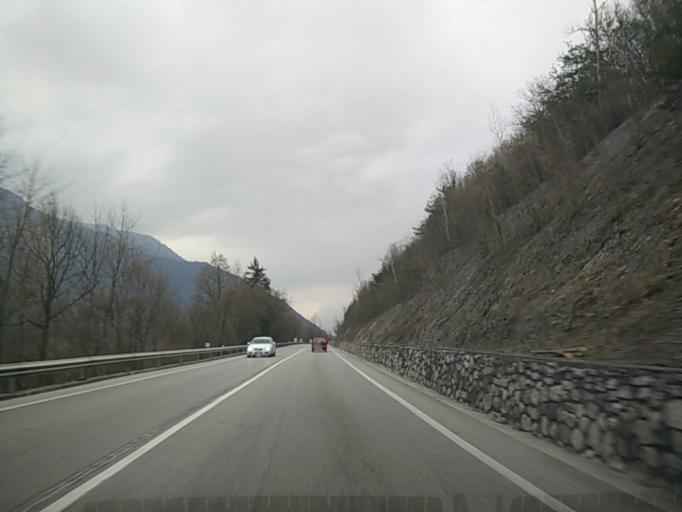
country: IT
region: Veneto
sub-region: Provincia di Belluno
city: Ponte nell'Alpi
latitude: 46.1666
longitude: 12.2702
